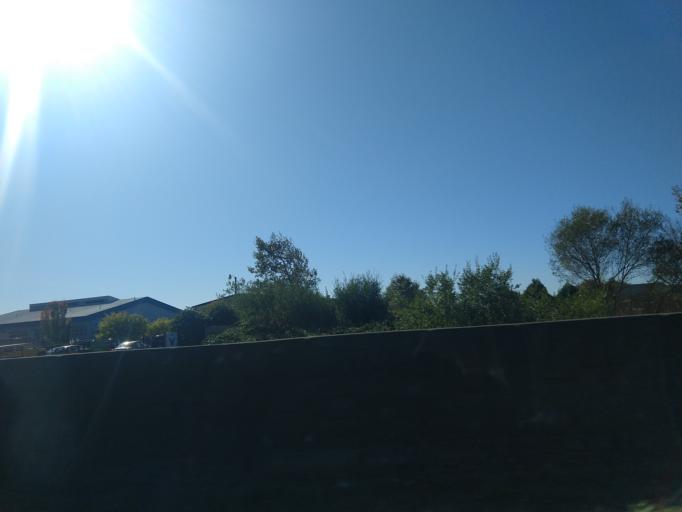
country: US
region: California
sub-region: Humboldt County
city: Fortuna
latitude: 40.5807
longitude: -124.1507
